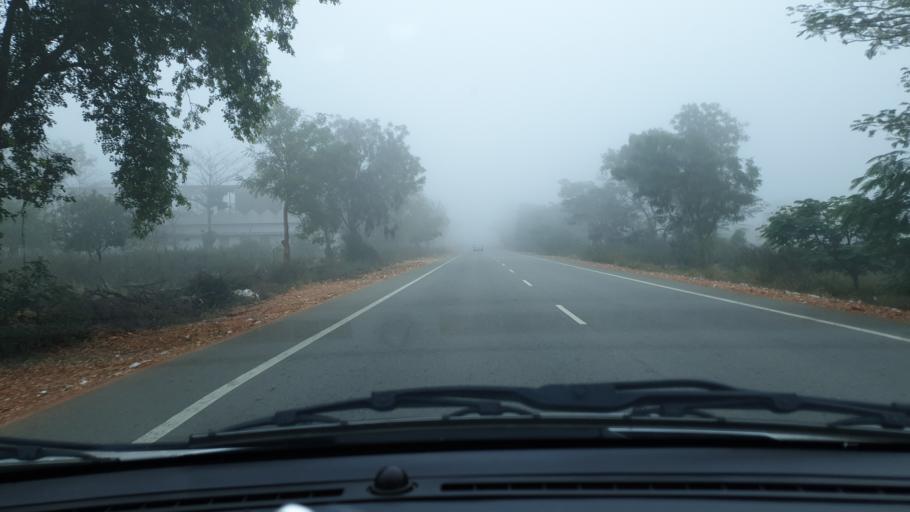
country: IN
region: Telangana
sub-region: Mahbubnagar
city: Nagar Karnul
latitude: 16.6401
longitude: 78.5938
